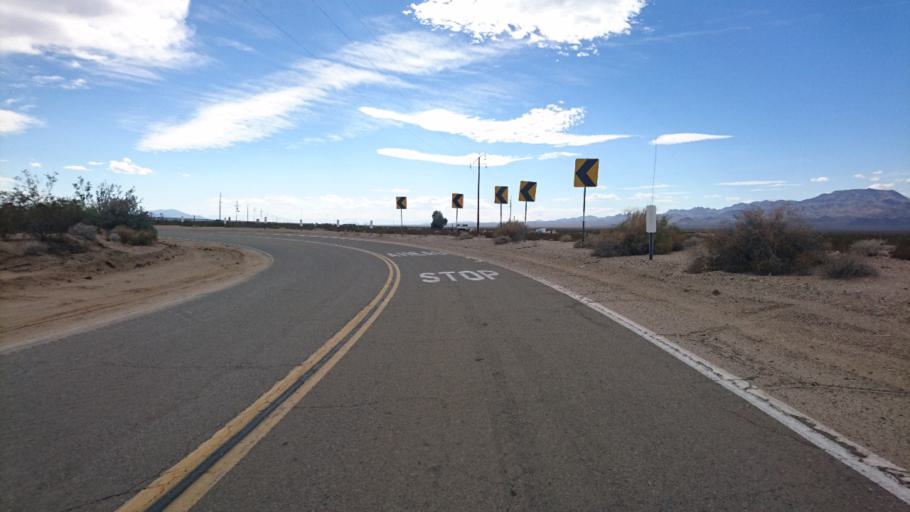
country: US
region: California
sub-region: San Bernardino County
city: Needles
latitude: 34.7534
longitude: -115.2247
